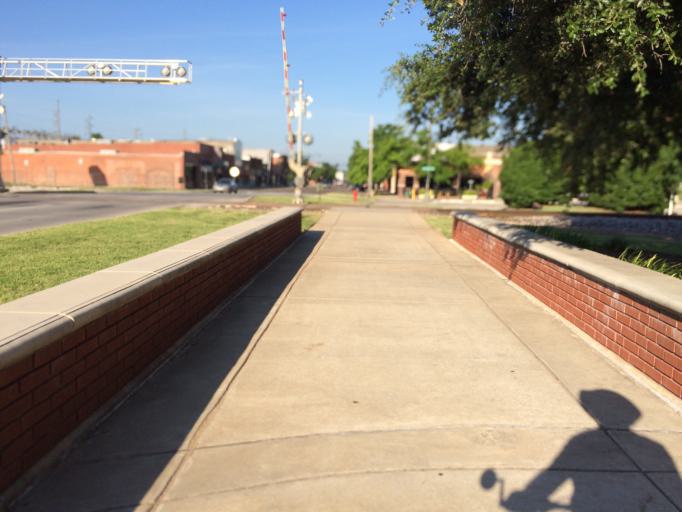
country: US
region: Oklahoma
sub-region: Cleveland County
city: Norman
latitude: 35.2211
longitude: -97.4434
